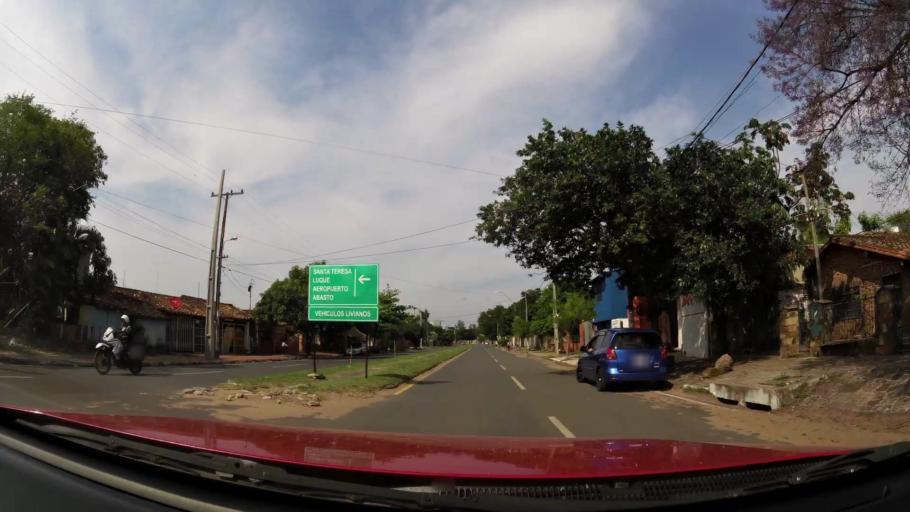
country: PY
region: Central
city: Fernando de la Mora
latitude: -25.2747
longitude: -57.5500
